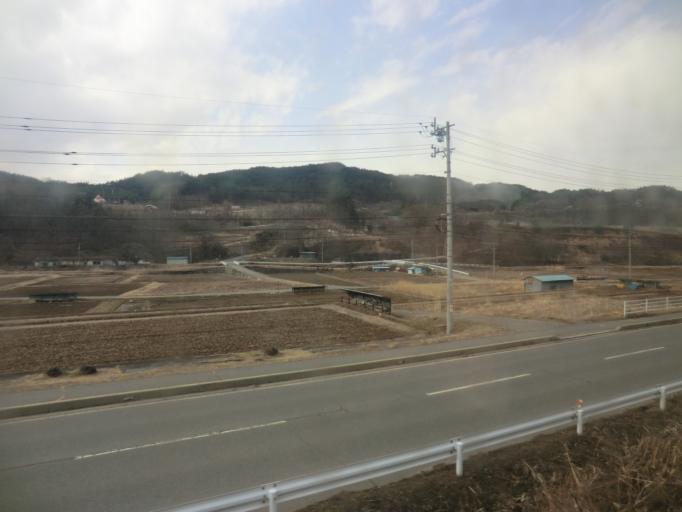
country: JP
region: Nagano
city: Hotaka
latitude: 36.4239
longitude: 138.0125
